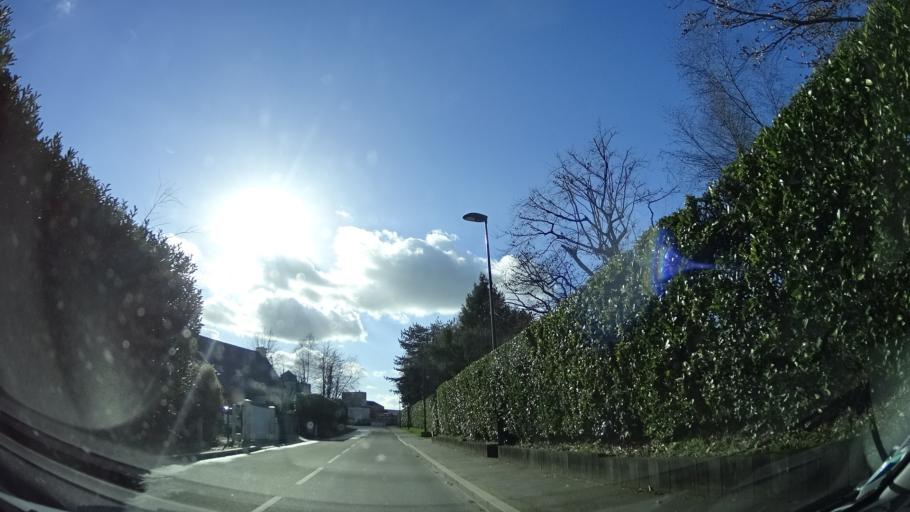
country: FR
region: Brittany
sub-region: Departement d'Ille-et-Vilaine
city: Pace
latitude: 48.1491
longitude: -1.7617
